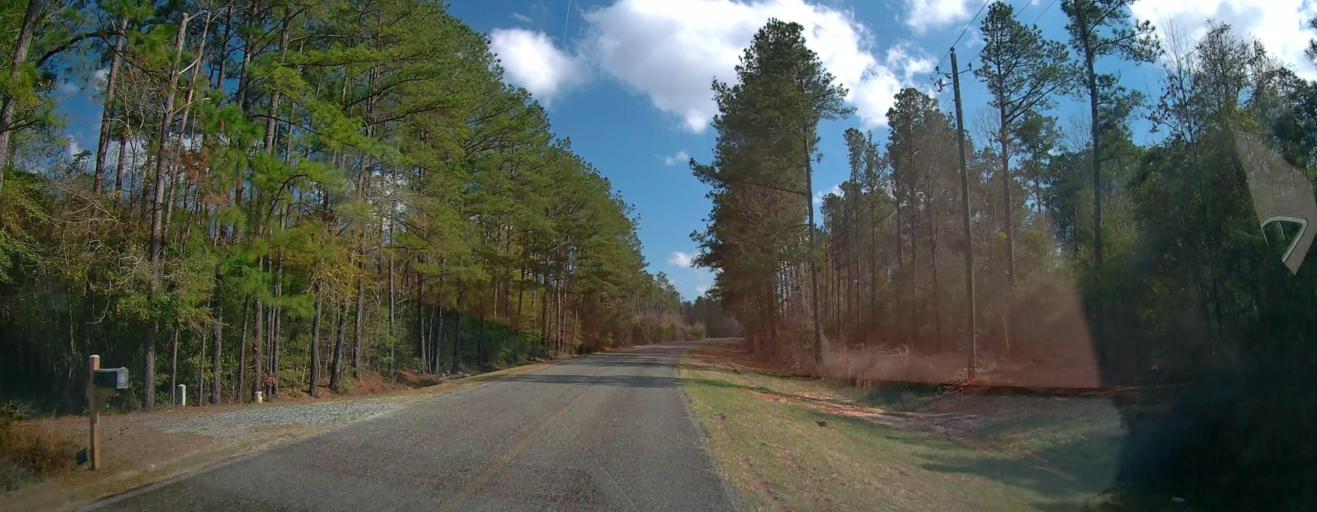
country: US
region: Georgia
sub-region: Twiggs County
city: Jeffersonville
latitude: 32.6718
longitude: -83.2368
